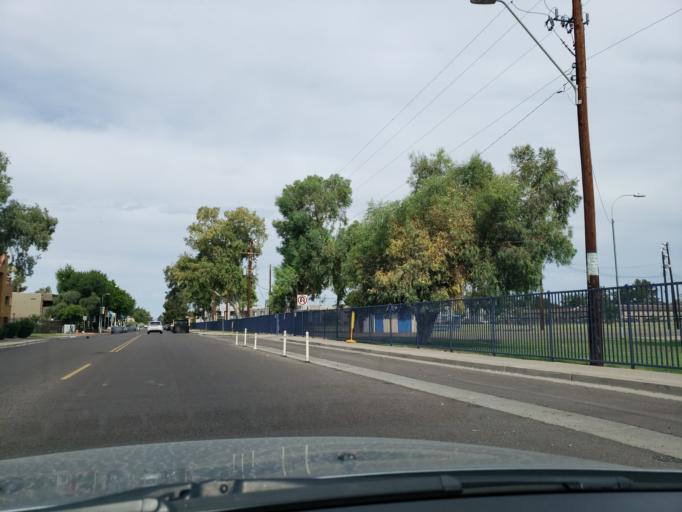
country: US
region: Arizona
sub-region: Maricopa County
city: Glendale
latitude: 33.5604
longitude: -112.1021
